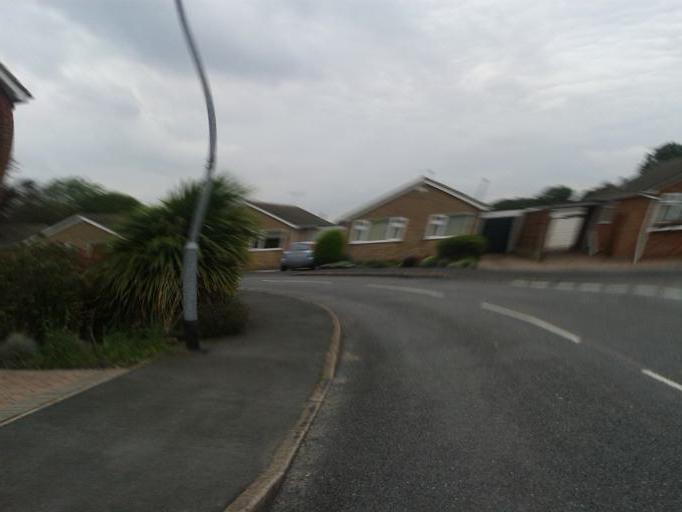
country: GB
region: England
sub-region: Leicestershire
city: Hinckley
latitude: 52.5526
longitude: -1.3556
